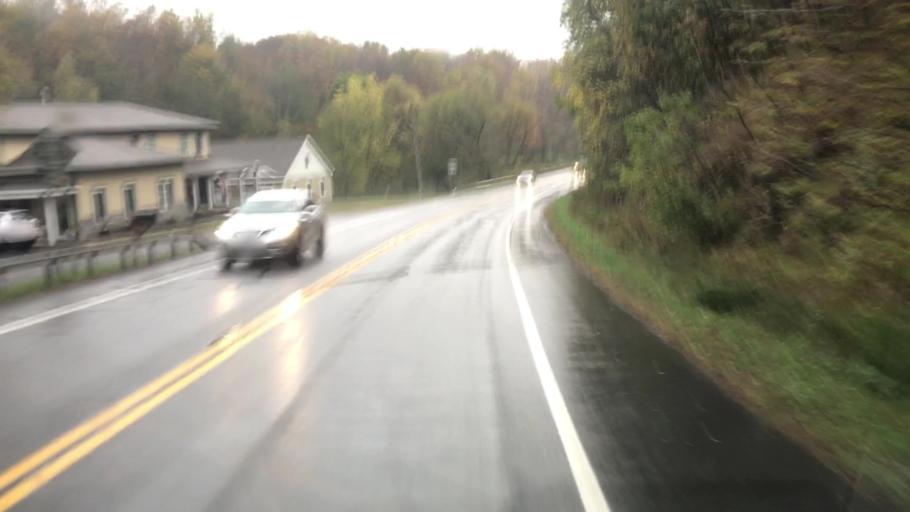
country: US
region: New York
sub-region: Onondaga County
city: Marcellus
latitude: 42.9982
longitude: -76.3408
